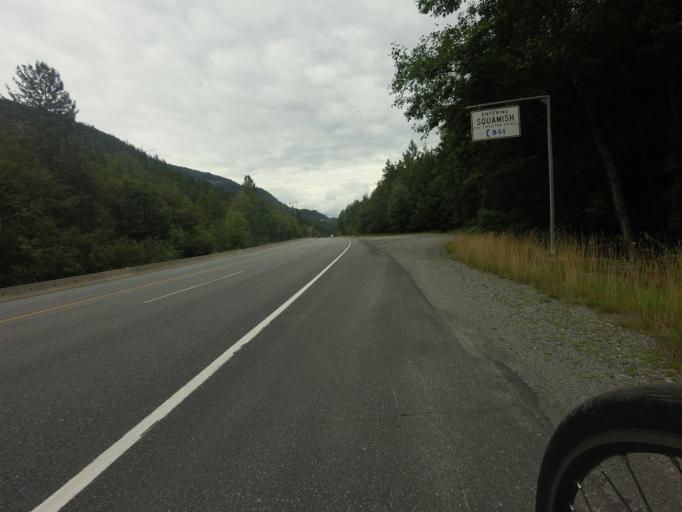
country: CA
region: British Columbia
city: Whistler
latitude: 49.8671
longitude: -123.1611
